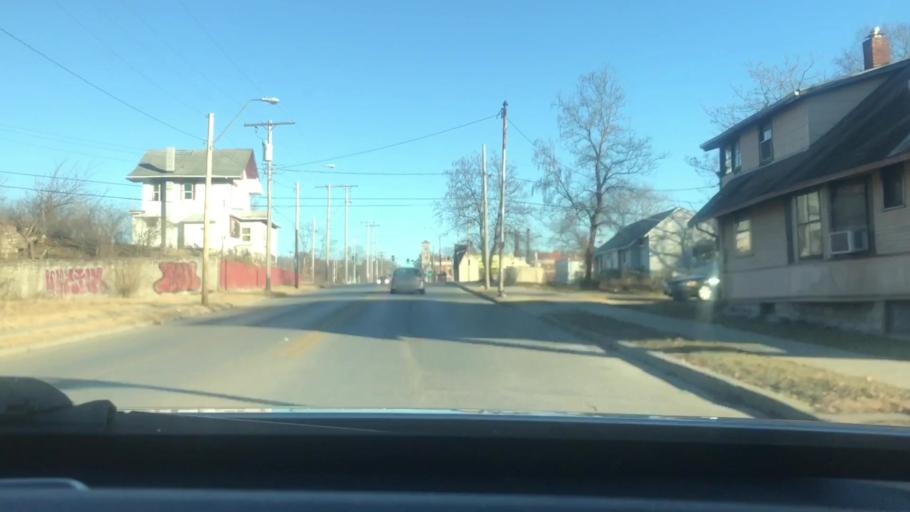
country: US
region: Missouri
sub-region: Jackson County
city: Kansas City
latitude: 39.0555
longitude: -94.5558
